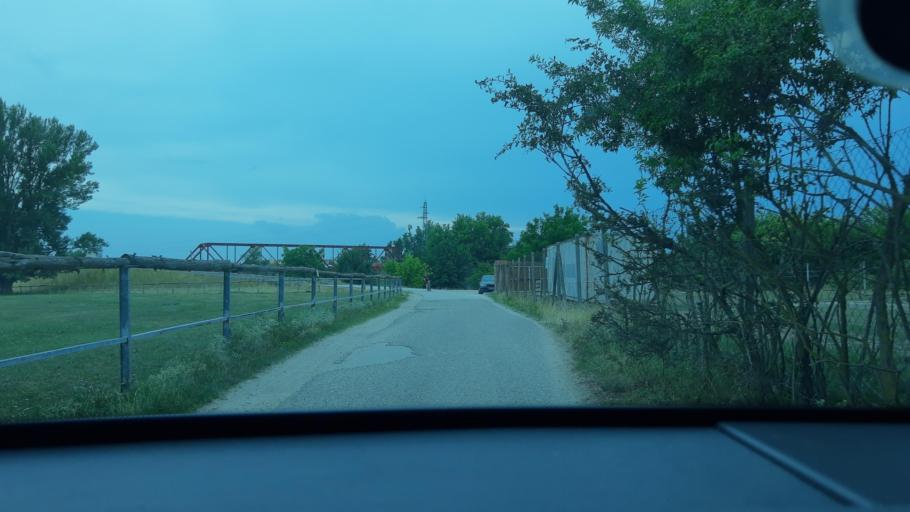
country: SK
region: Trnavsky
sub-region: Okres Trnava
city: Piestany
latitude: 48.6073
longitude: 17.8420
